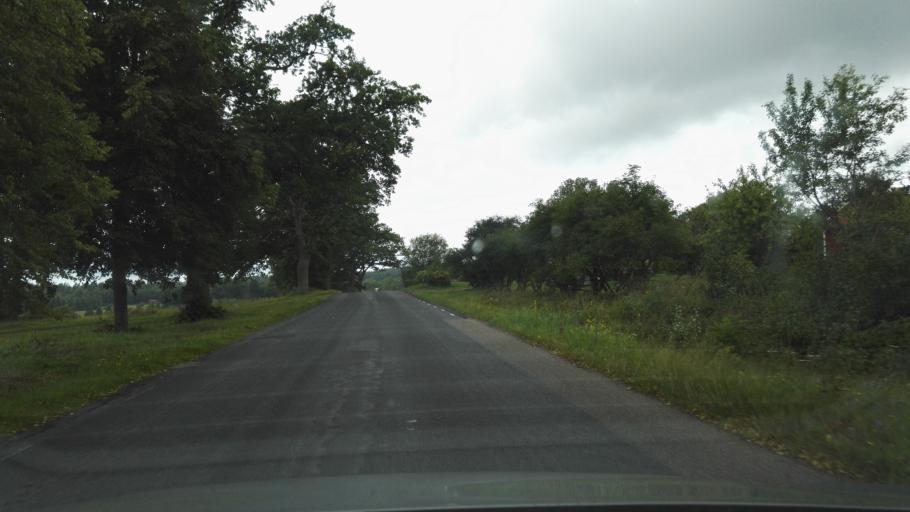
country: SE
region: Kronoberg
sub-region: Vaxjo Kommun
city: Rottne
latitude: 57.0882
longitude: 14.8127
